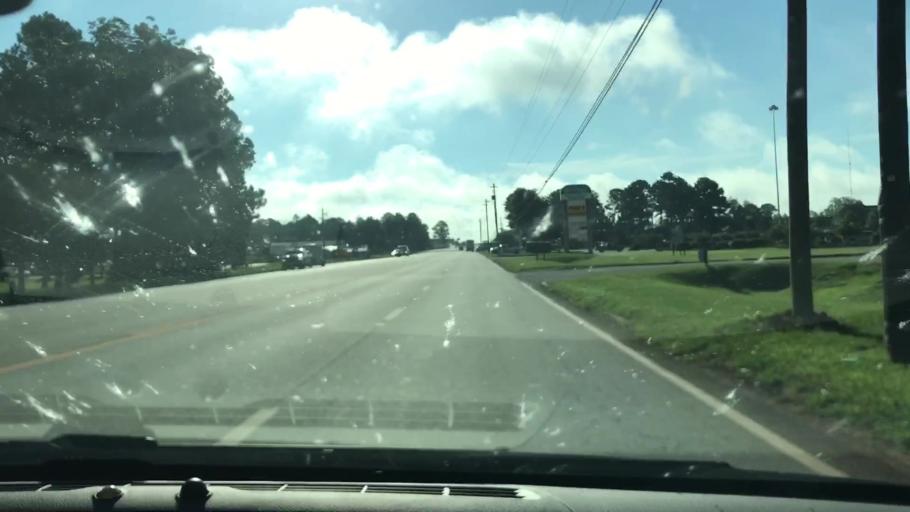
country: US
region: Georgia
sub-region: Terrell County
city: Dawson
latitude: 31.7622
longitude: -84.4403
